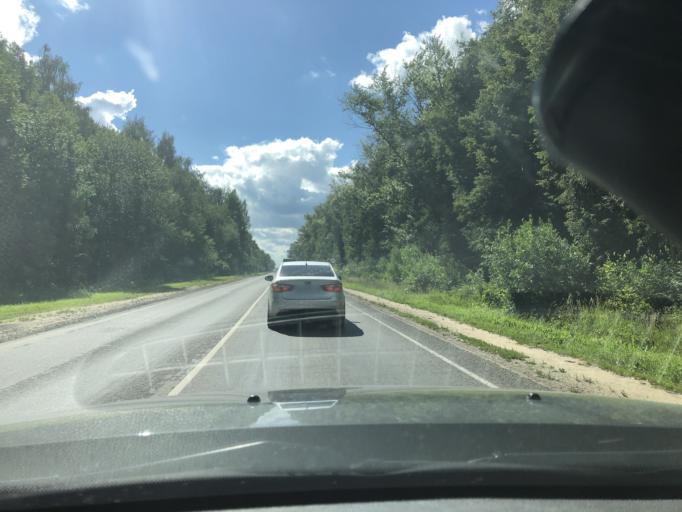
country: RU
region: Tula
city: Severo-Zadonsk
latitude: 53.9705
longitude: 38.4155
